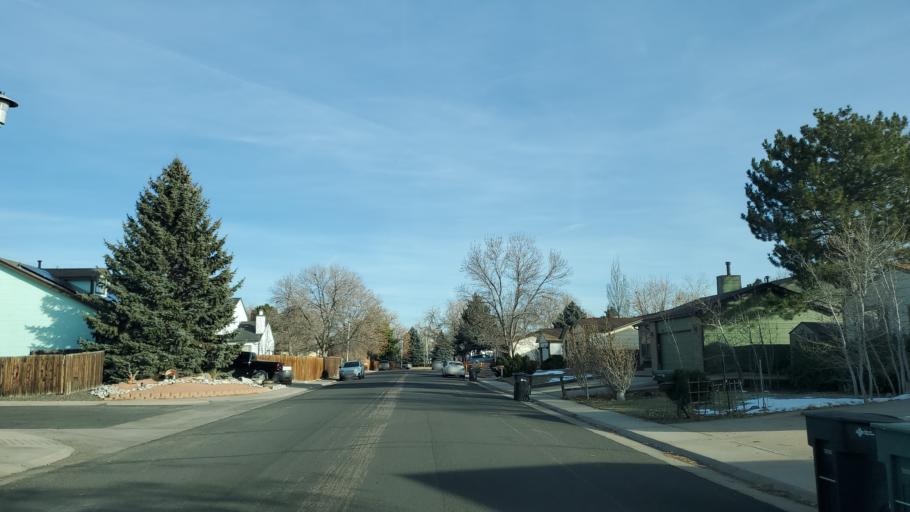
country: US
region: Colorado
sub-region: Adams County
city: Northglenn
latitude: 39.9060
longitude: -104.9523
